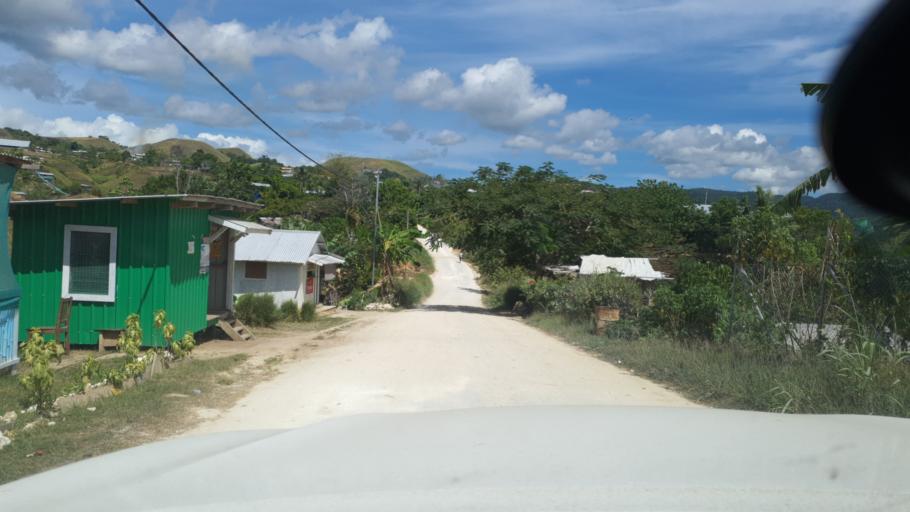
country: SB
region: Guadalcanal
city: Honiara
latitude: -9.4345
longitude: 159.9254
